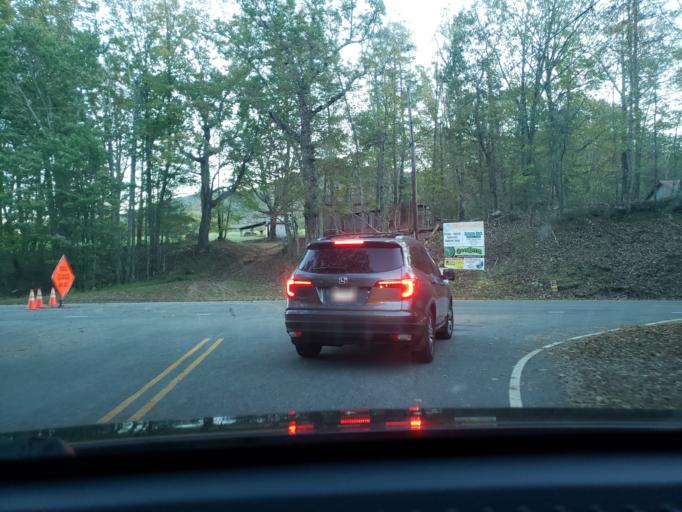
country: US
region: North Carolina
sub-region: Stokes County
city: Danbury
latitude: 36.4150
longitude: -80.2452
